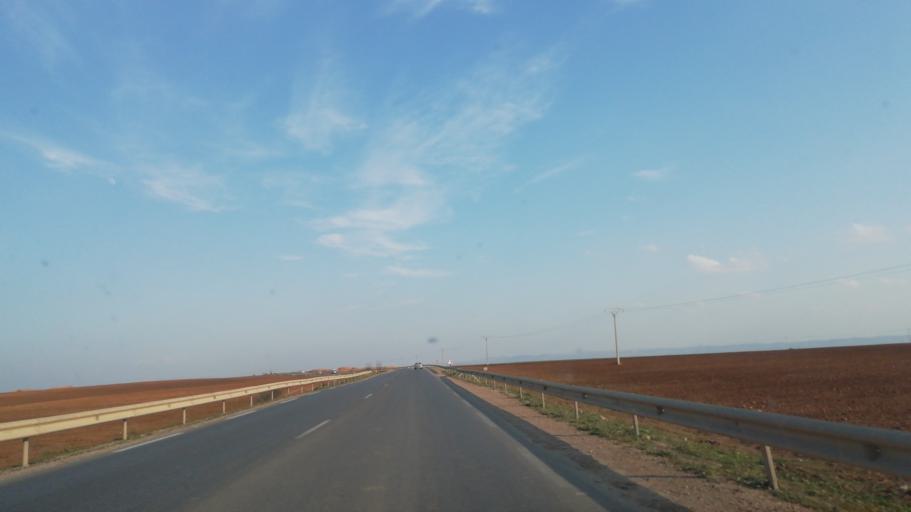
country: DZ
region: Relizane
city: Relizane
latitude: 35.8922
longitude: 0.6183
